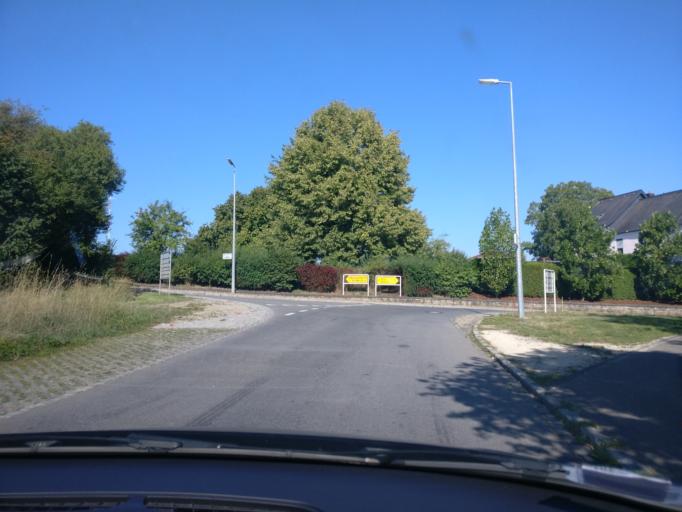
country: LU
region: Grevenmacher
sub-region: Canton de Grevenmacher
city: Betzdorf
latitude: 49.7180
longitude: 6.3079
